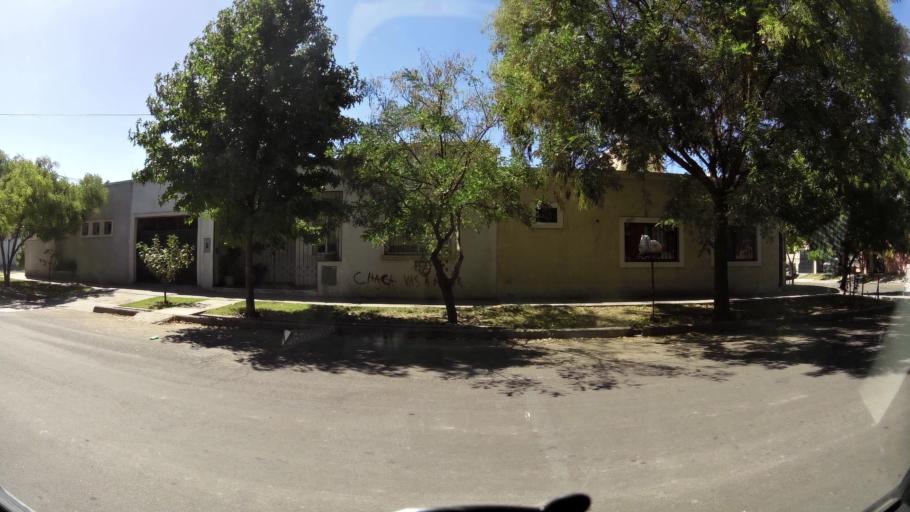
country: AR
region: Mendoza
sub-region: Departamento de Godoy Cruz
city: Godoy Cruz
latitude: -32.9767
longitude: -68.8561
